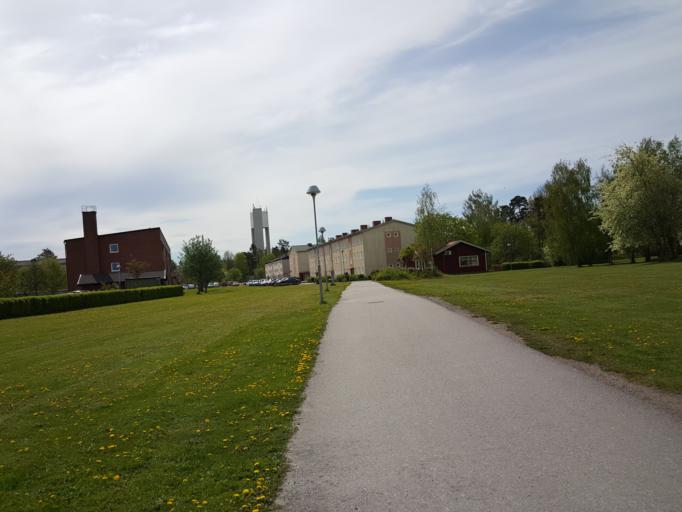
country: SE
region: Uppsala
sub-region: Osthammars Kommun
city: Gimo
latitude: 60.1749
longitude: 18.1831
